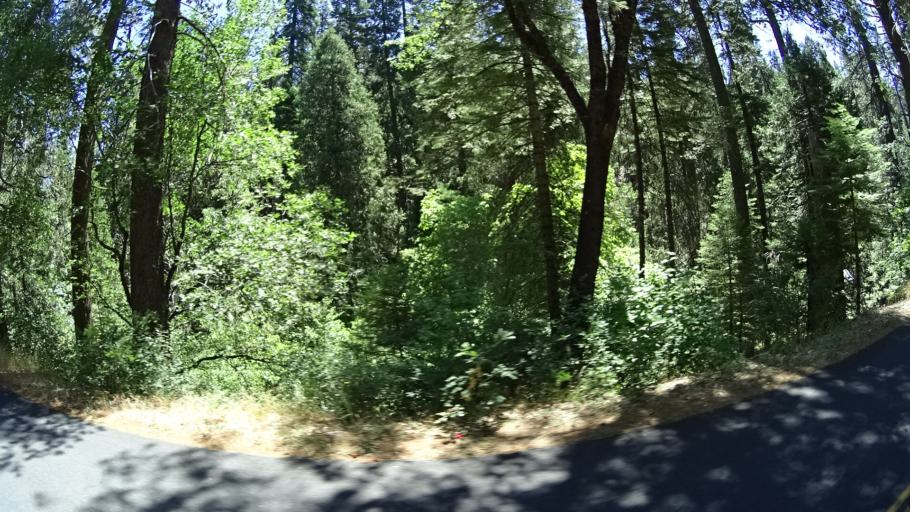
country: US
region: California
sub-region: Calaveras County
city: Arnold
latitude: 38.2311
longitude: -120.3546
